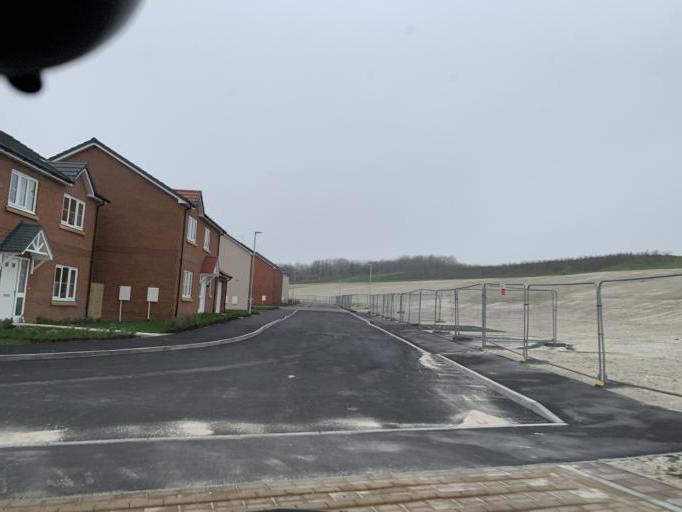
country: GB
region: England
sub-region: Wiltshire
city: Durrington
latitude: 51.2008
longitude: -1.7970
